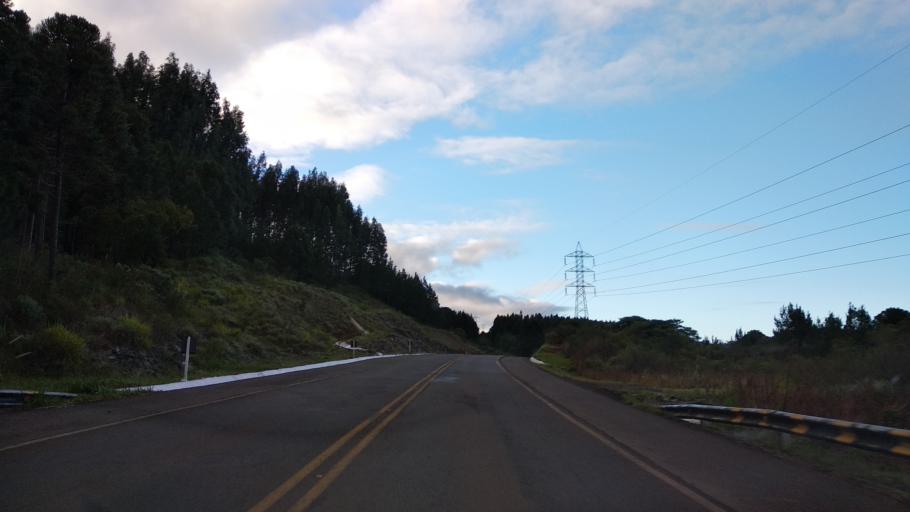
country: BR
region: Santa Catarina
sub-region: Curitibanos
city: Curitibanos
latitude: -27.5476
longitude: -50.8480
